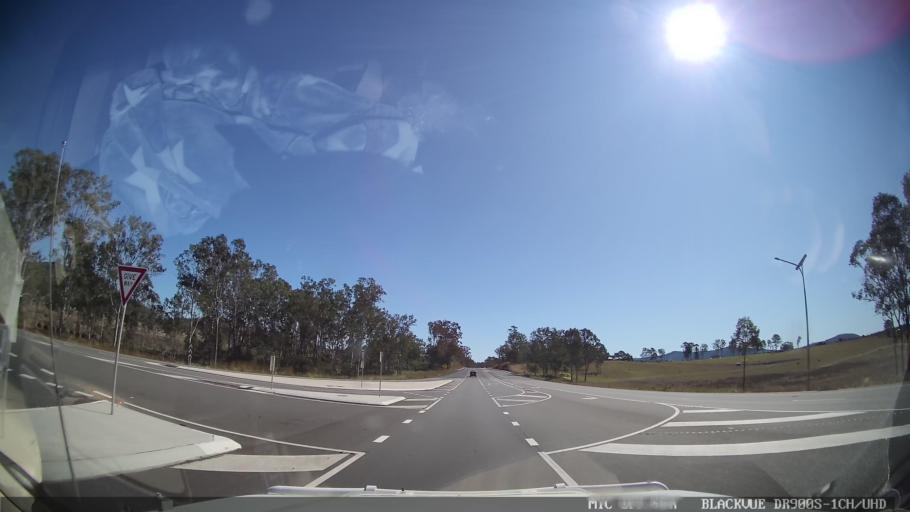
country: AU
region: Queensland
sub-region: Gympie Regional Council
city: Gympie
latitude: -26.0349
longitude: 152.5680
